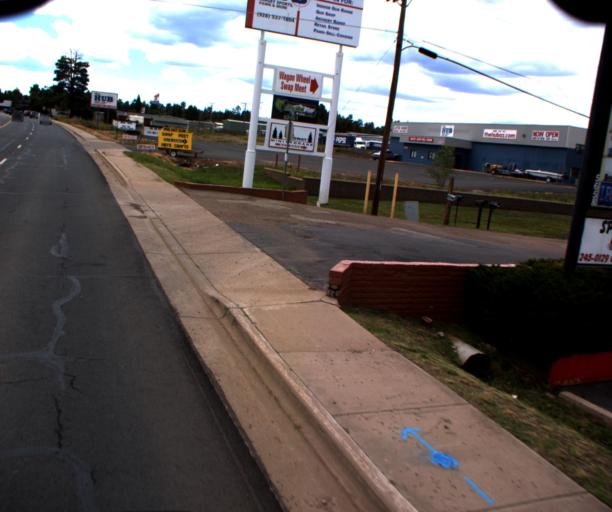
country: US
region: Arizona
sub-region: Navajo County
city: Lake of the Woods
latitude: 34.1882
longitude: -110.0158
